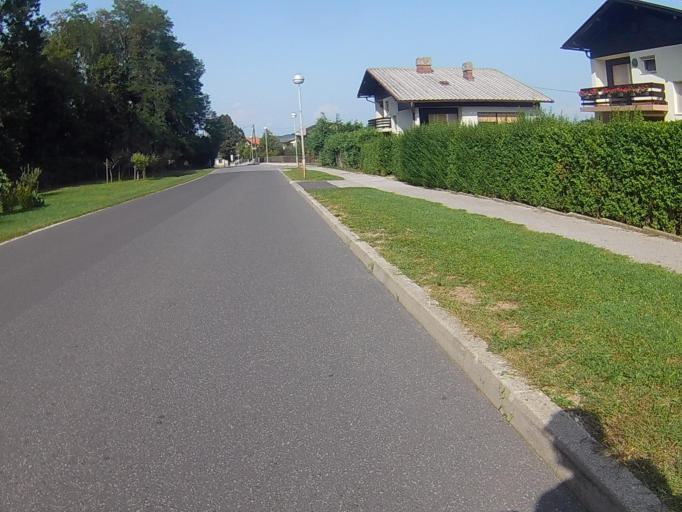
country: SI
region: Maribor
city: Pekre
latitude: 46.5450
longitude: 15.5927
